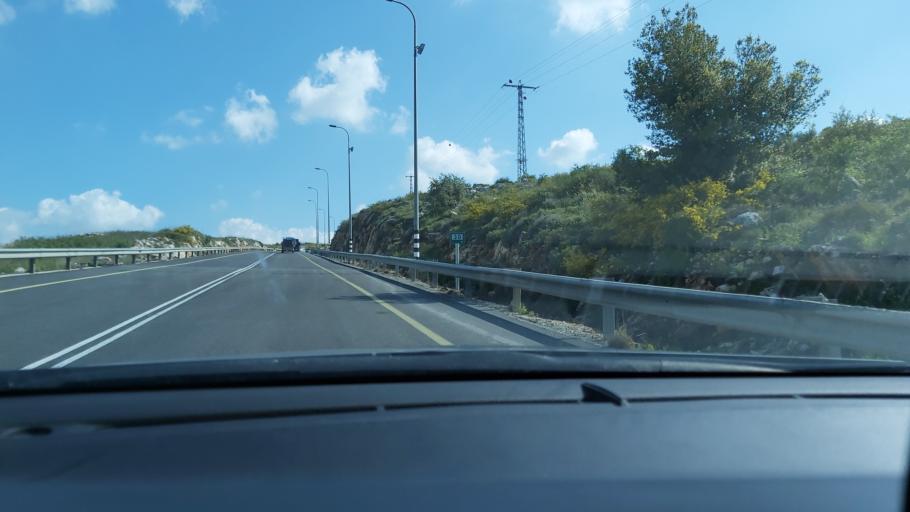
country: PS
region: West Bank
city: Bruqin
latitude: 32.0877
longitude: 35.1034
